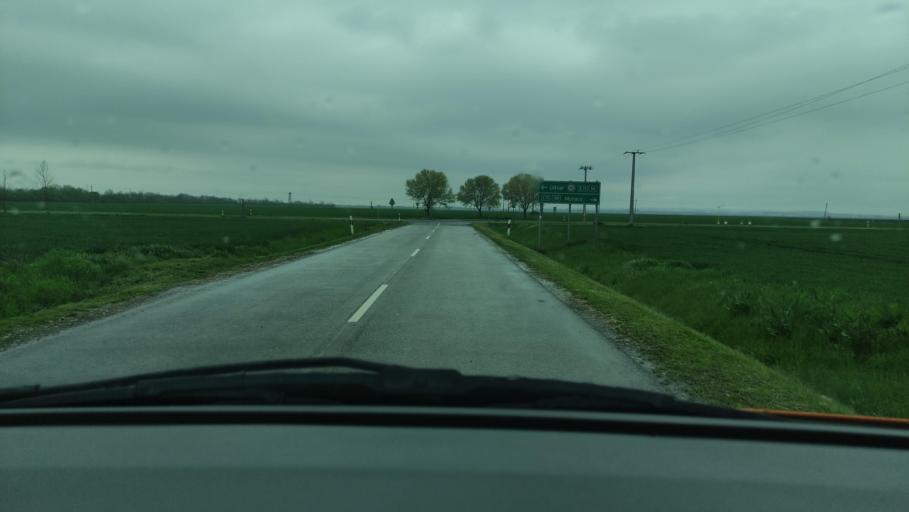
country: HU
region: Baranya
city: Mohacs
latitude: 45.9515
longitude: 18.6685
